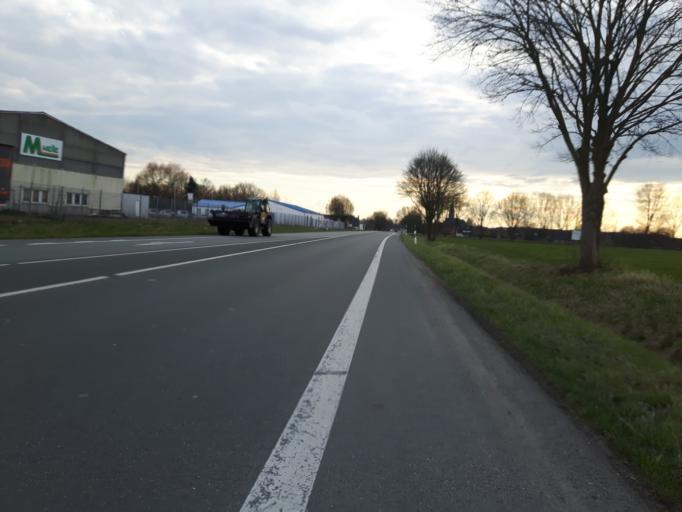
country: DE
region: North Rhine-Westphalia
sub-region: Regierungsbezirk Munster
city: Nottuln
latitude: 51.8706
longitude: 7.3800
